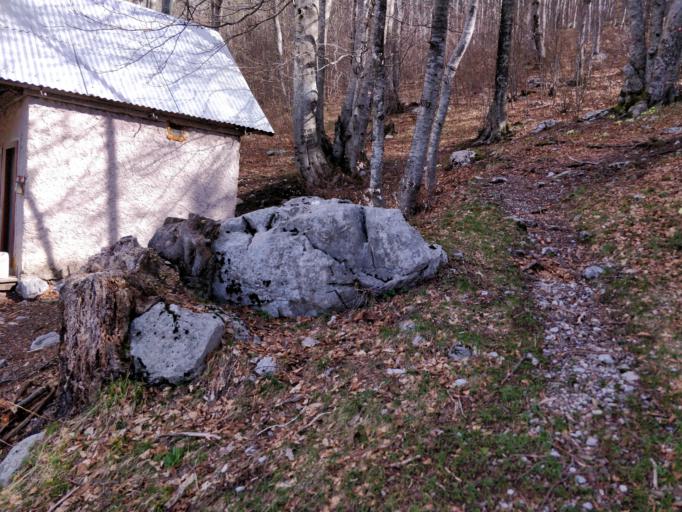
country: HR
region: Zadarska
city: Starigrad
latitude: 44.3366
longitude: 15.5368
